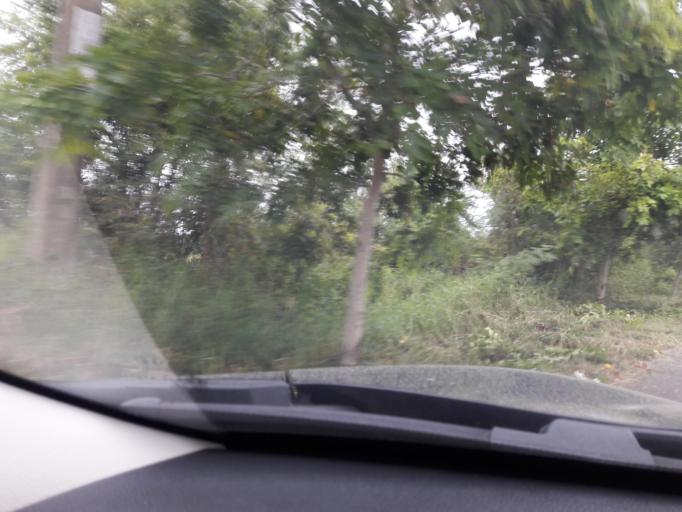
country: TH
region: Ratchaburi
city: Bang Phae
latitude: 13.6275
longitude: 99.9485
